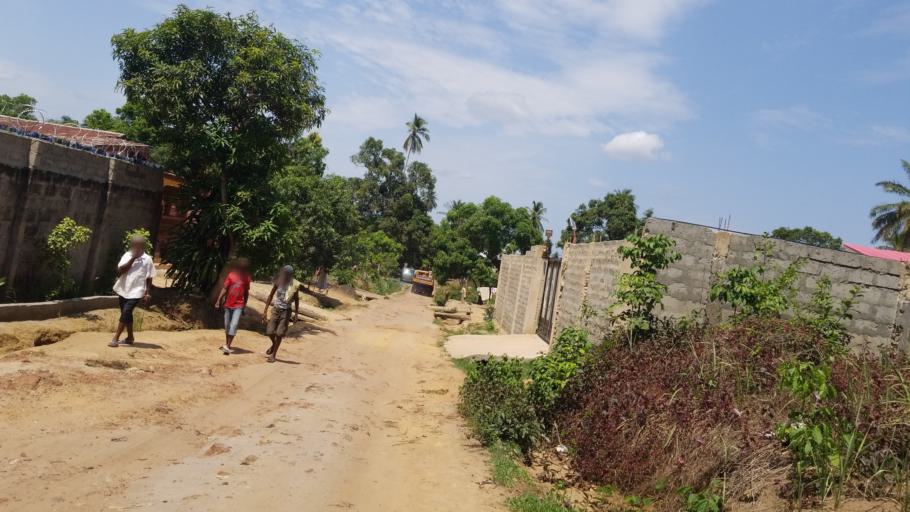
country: SL
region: Western Area
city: Waterloo
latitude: 8.3071
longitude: -13.0502
